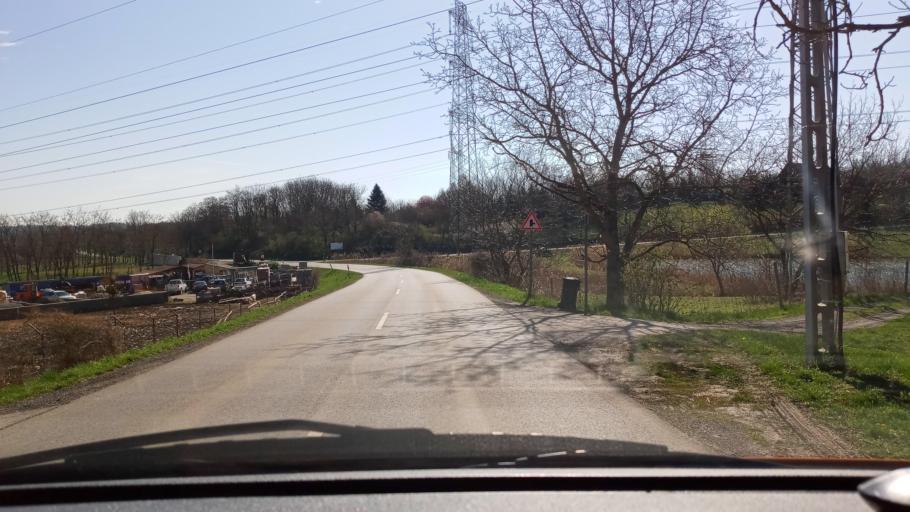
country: HU
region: Baranya
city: Kozarmisleny
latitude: 46.0845
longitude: 18.3061
